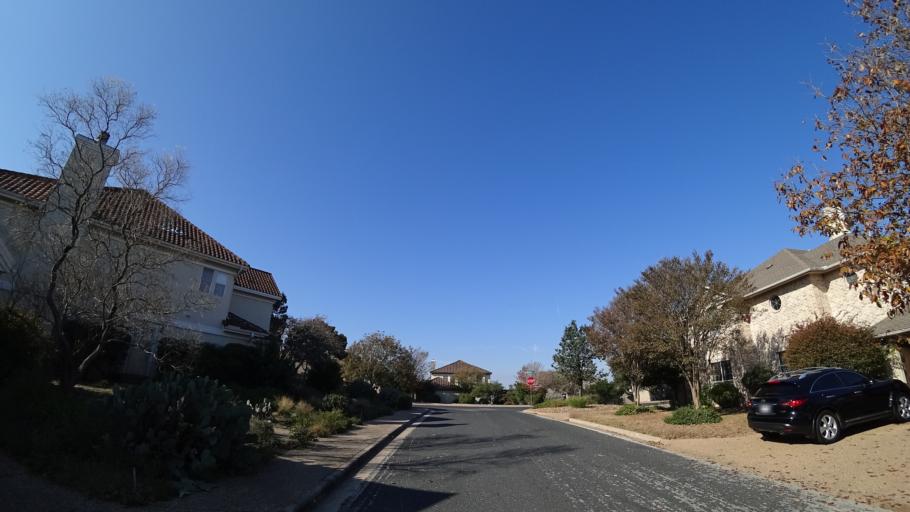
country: US
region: Texas
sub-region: Williamson County
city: Jollyville
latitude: 30.3919
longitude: -97.7690
